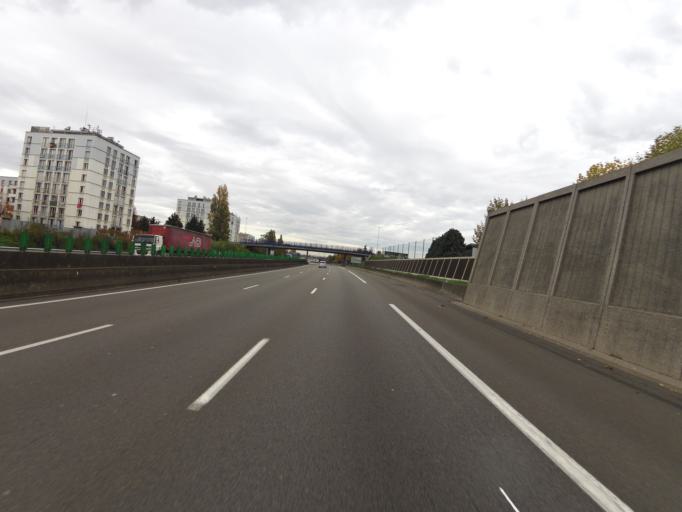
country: FR
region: Rhone-Alpes
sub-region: Departement du Rhone
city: Villefranche-sur-Saone
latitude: 45.9808
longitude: 4.7369
